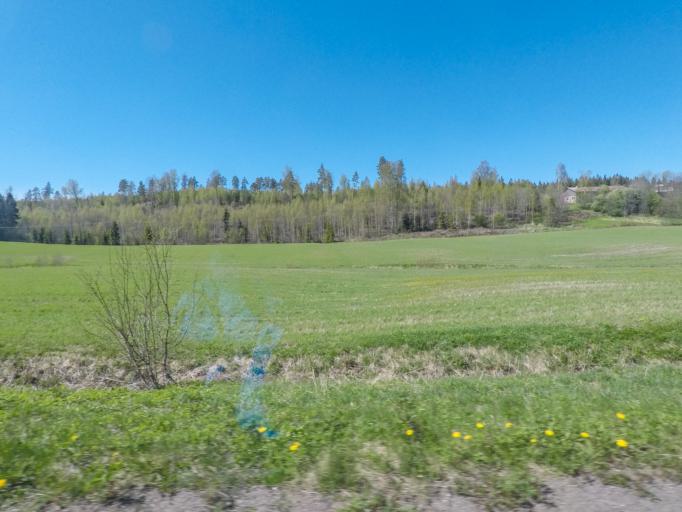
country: FI
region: Uusimaa
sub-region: Helsinki
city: Sammatti
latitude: 60.4107
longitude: 23.8227
